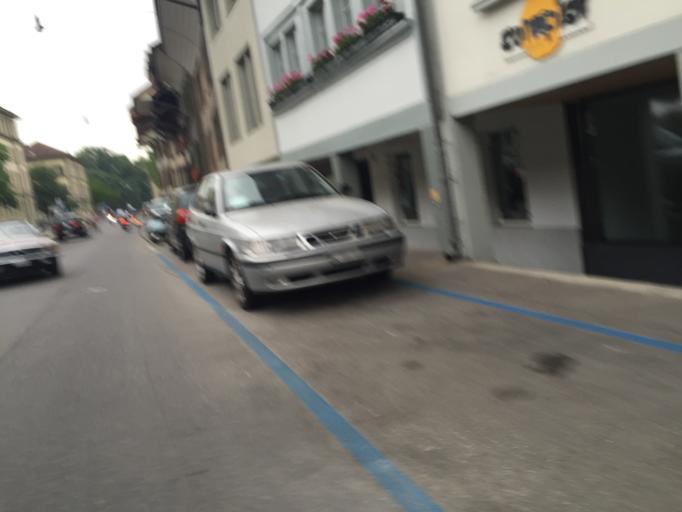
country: CH
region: Bern
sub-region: Bern-Mittelland District
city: Bern
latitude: 46.9473
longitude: 7.4564
